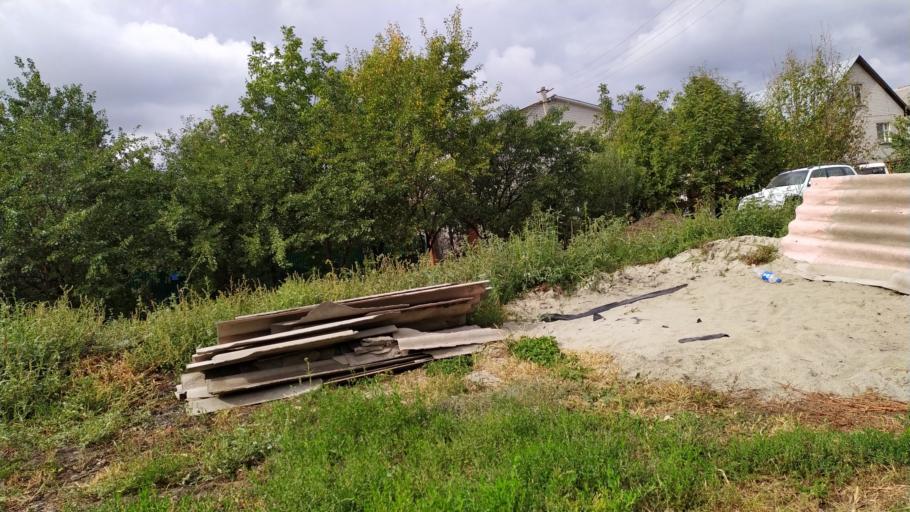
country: RU
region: Kursk
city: Kursk
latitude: 51.6401
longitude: 36.1390
